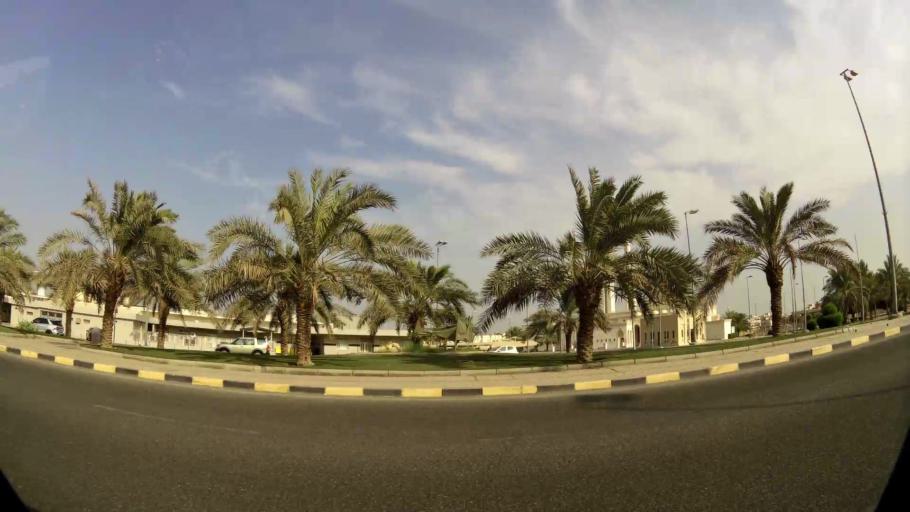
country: KW
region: Al Asimah
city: Ash Shamiyah
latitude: 29.3272
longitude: 47.9813
